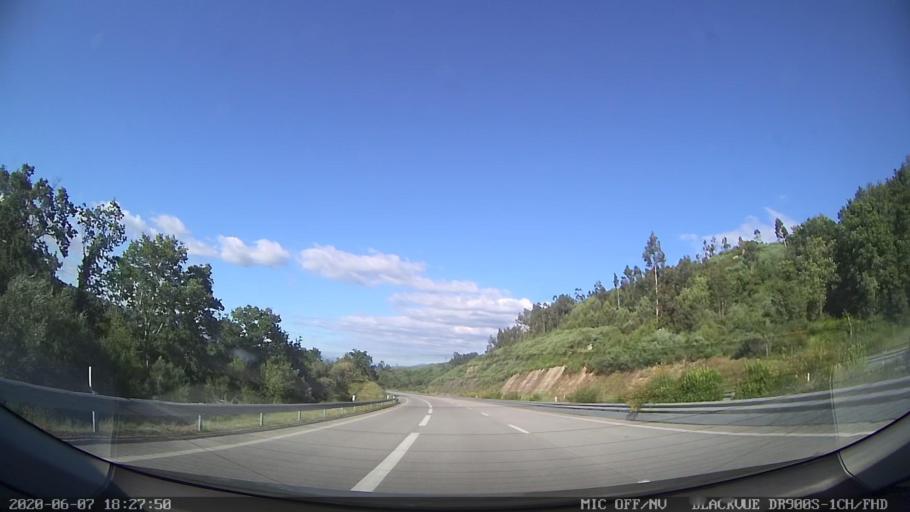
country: PT
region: Braga
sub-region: Celorico de Basto
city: Celorico de Basto
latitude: 41.4480
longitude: -8.0563
